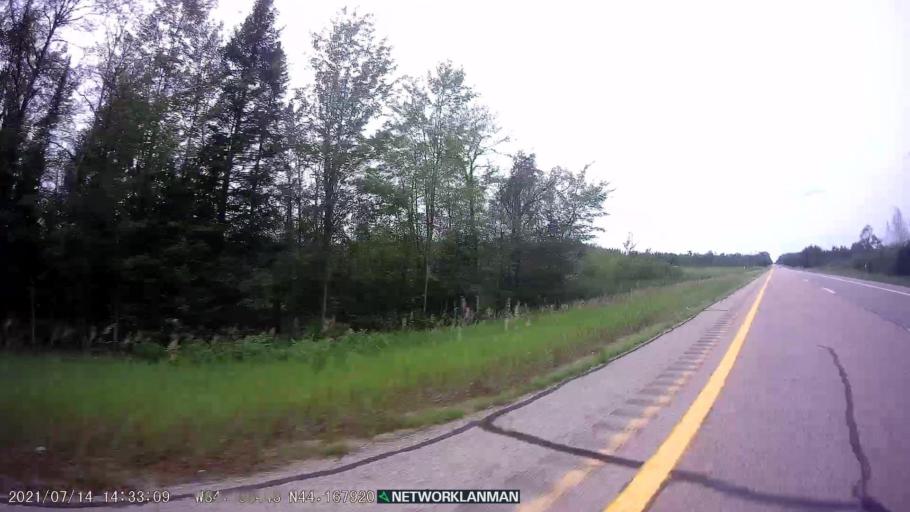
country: US
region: Michigan
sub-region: Clare County
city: Harrison
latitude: 44.1685
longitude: -84.7955
